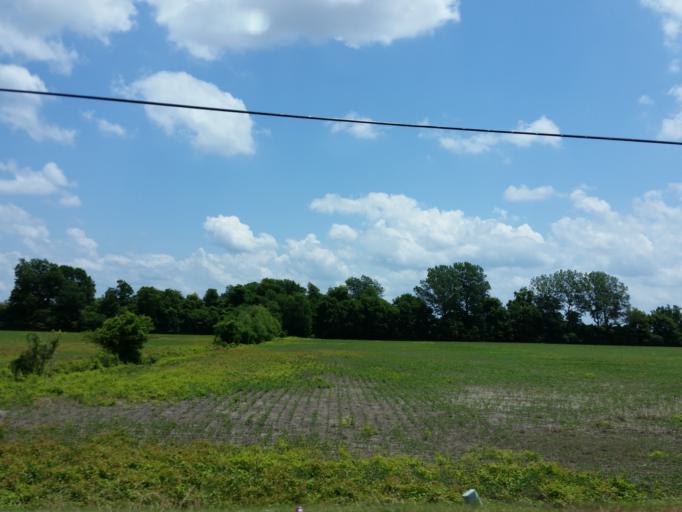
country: US
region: Tennessee
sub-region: Lake County
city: Tiptonville
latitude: 36.3646
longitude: -89.4686
